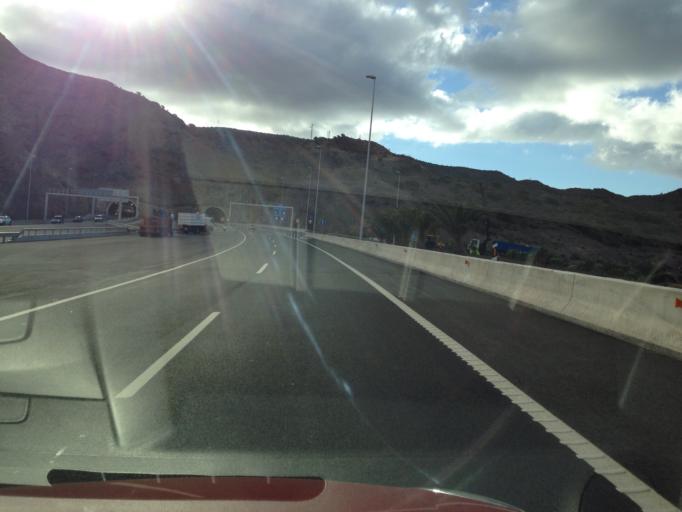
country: ES
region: Canary Islands
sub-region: Provincia de Las Palmas
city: Puerto Rico
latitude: 27.8018
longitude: -15.7071
